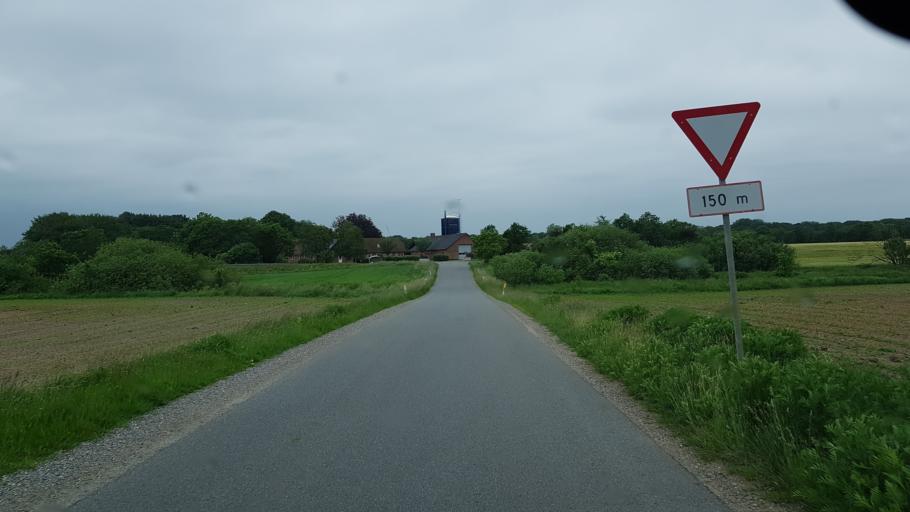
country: DK
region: South Denmark
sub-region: Varde Kommune
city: Olgod
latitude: 55.6684
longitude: 8.7375
